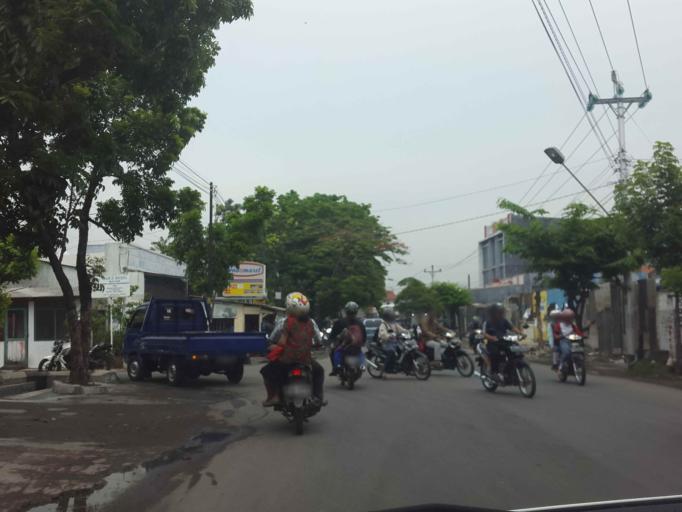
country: ID
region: Central Java
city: Semarang
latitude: -6.9972
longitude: 110.4461
